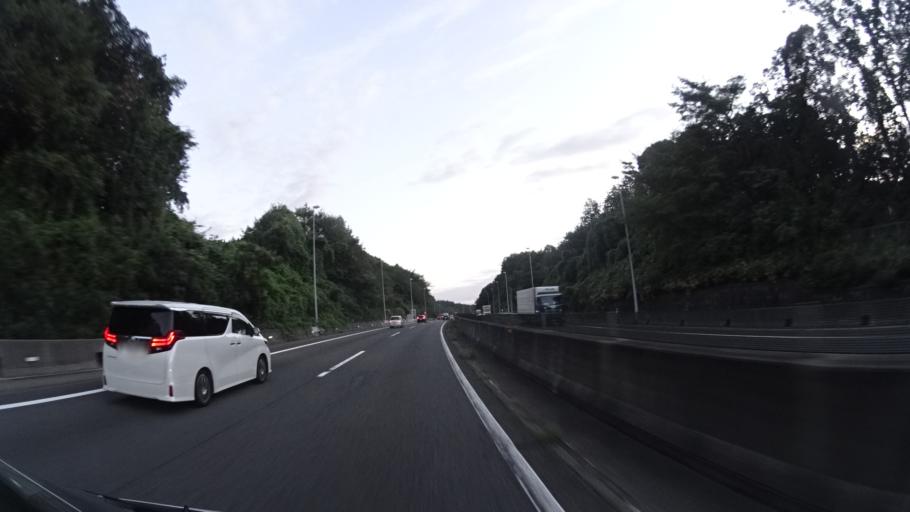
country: JP
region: Shiga Prefecture
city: Hikone
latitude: 35.1819
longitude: 136.2821
